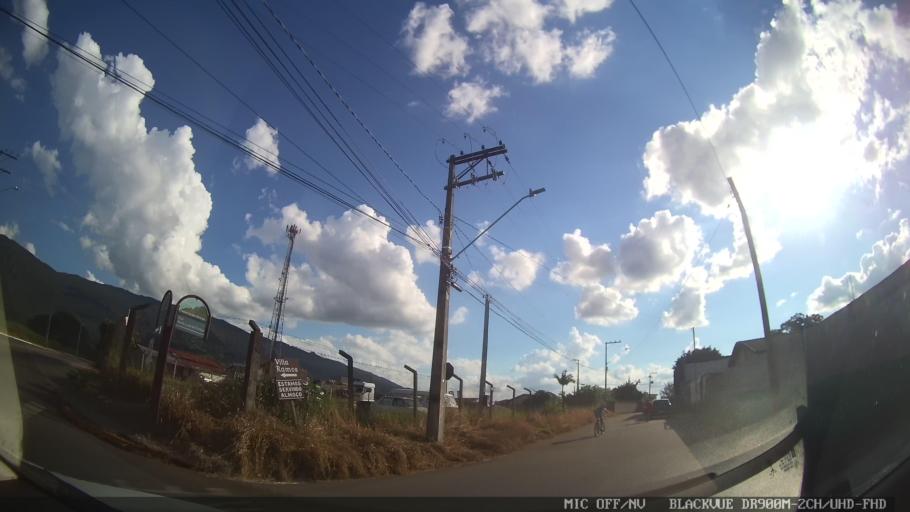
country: BR
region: Minas Gerais
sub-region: Extrema
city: Extrema
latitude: -22.8480
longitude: -46.3290
